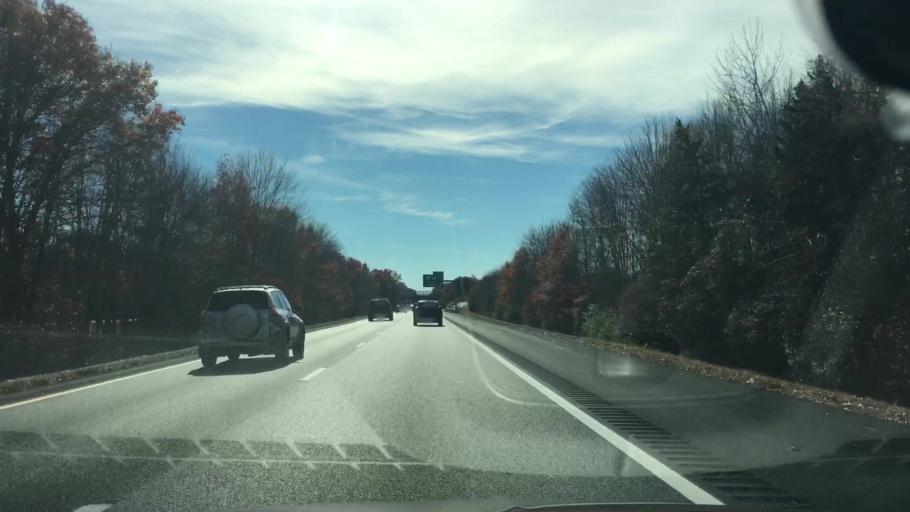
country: US
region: Massachusetts
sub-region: Franklin County
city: Whately
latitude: 42.4374
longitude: -72.6215
